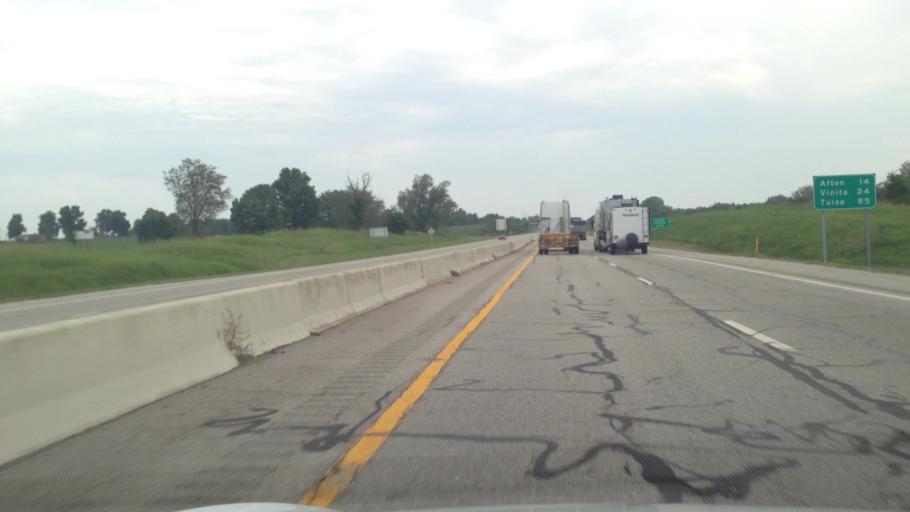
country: US
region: Oklahoma
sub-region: Ottawa County
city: Miami
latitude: 36.8502
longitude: -94.8567
